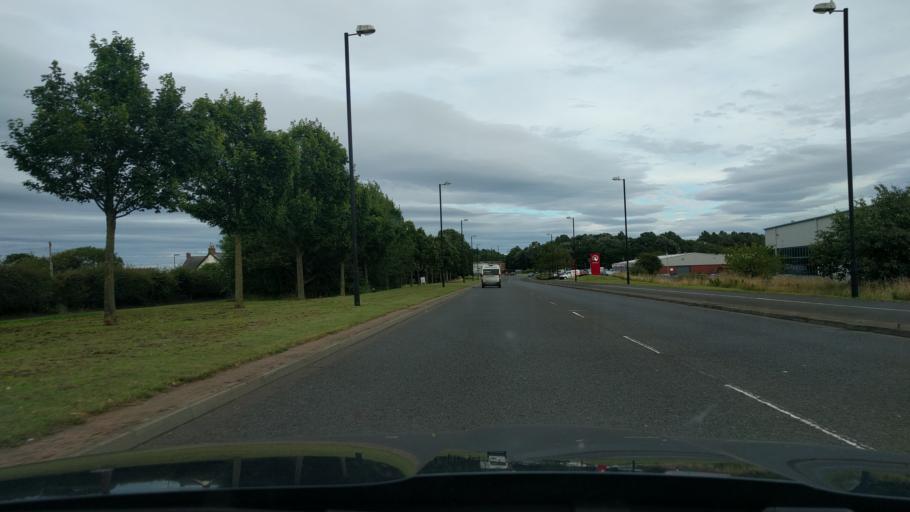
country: GB
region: England
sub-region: Borough of North Tyneside
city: Shiremoor
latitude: 55.0259
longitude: -1.4977
